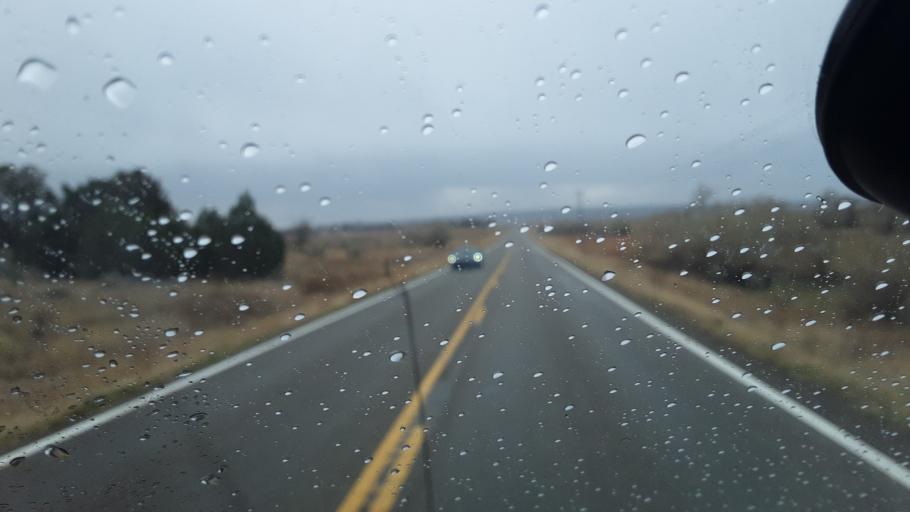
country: US
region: Colorado
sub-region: Montezuma County
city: Mancos
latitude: 37.1061
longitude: -108.1614
